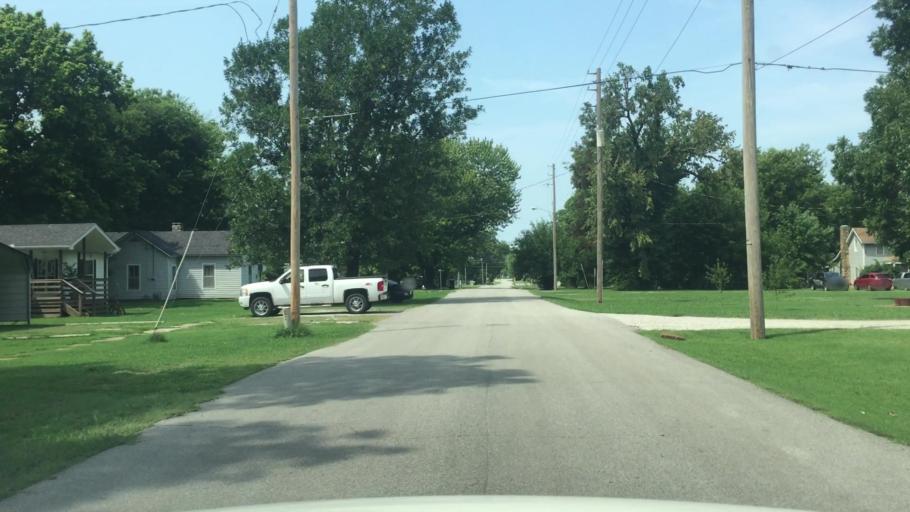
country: US
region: Kansas
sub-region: Labette County
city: Oswego
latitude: 37.1628
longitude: -95.1051
